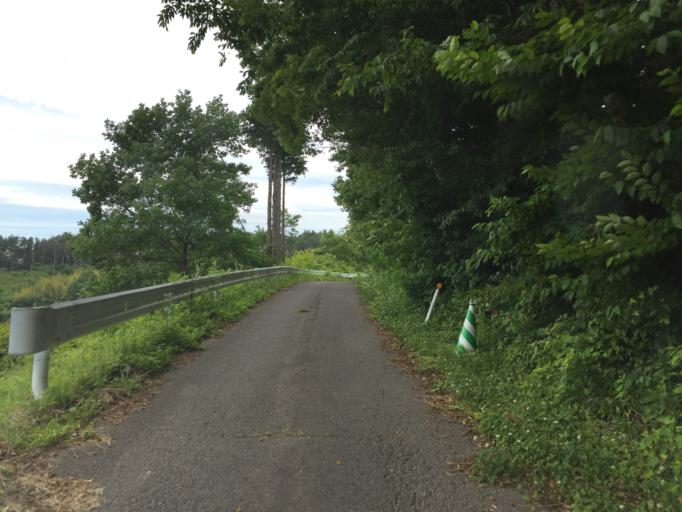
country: JP
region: Fukushima
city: Funehikimachi-funehiki
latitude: 37.4076
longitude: 140.6986
